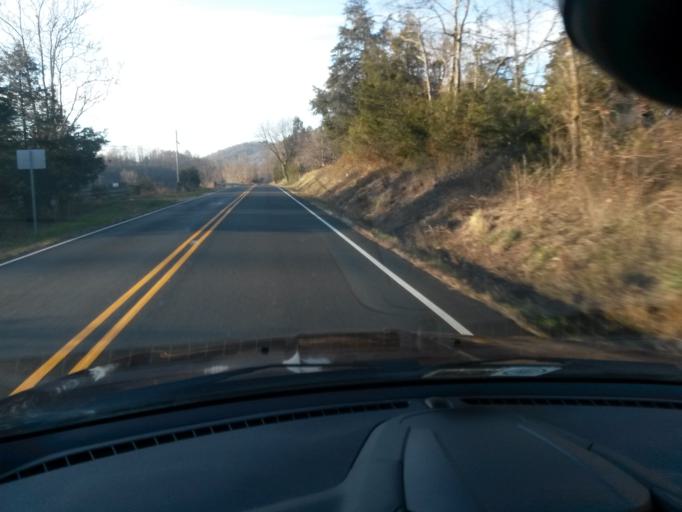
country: US
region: Virginia
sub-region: Amherst County
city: Amherst
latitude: 37.6609
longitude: -79.1560
